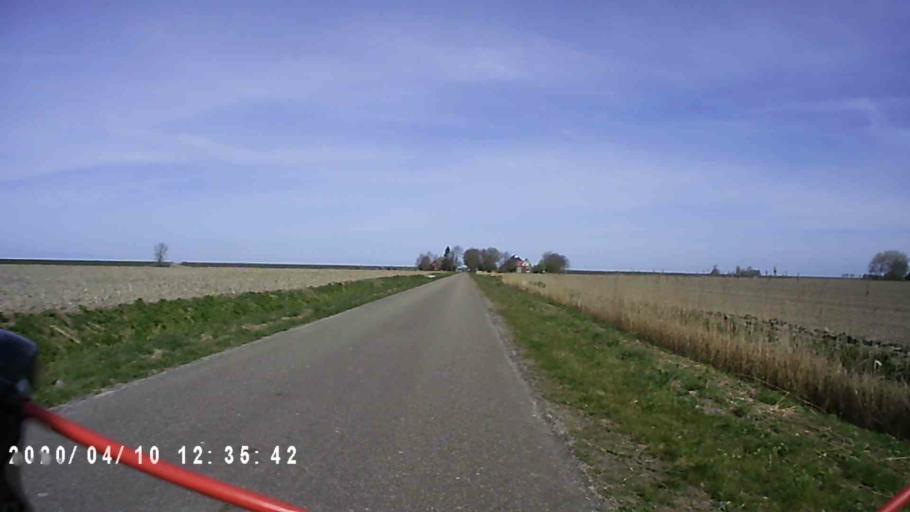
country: NL
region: Groningen
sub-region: Gemeente De Marne
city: Ulrum
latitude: 53.4008
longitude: 6.4174
